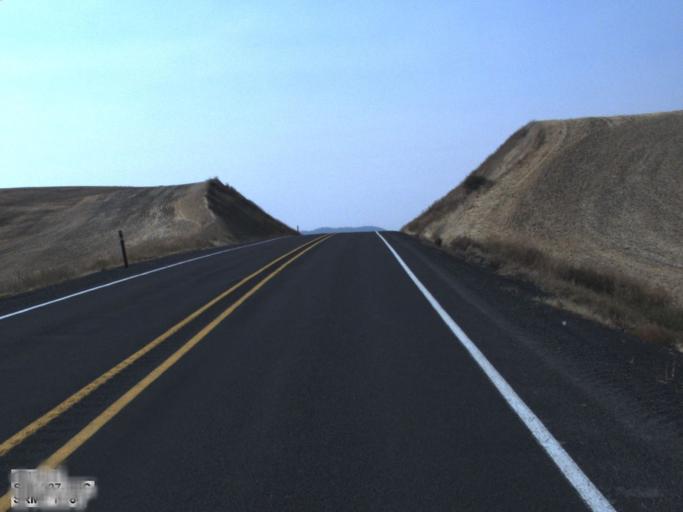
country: US
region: Idaho
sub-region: Latah County
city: Moscow
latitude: 46.9508
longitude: -117.0907
